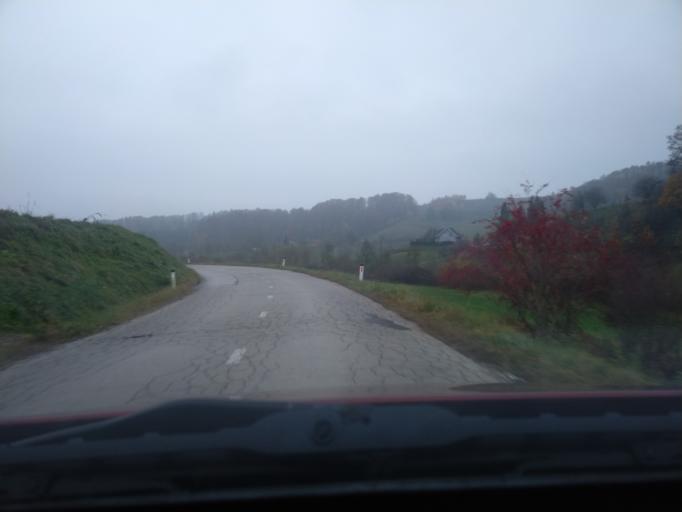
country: SI
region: Kungota
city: Zgornja Kungota
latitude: 46.6640
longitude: 15.6105
